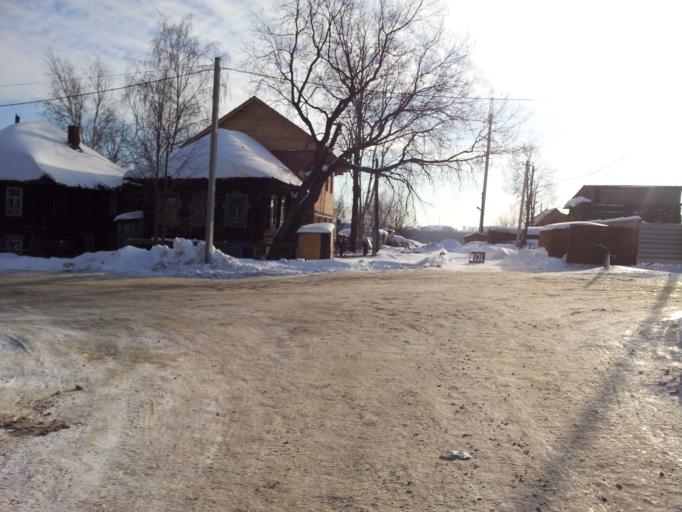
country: RU
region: Perm
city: Perm
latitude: 58.0209
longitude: 56.2637
